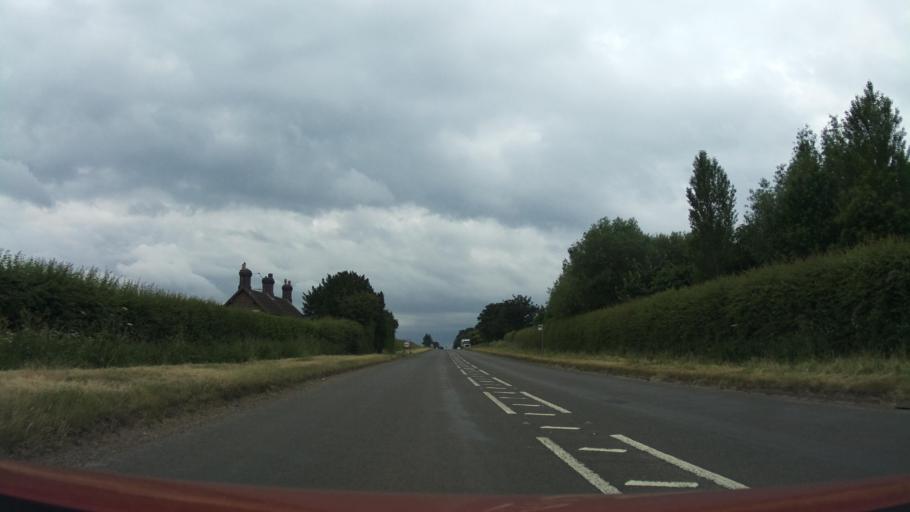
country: GB
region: England
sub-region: Staffordshire
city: Penkridge
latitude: 52.7434
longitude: -2.1081
